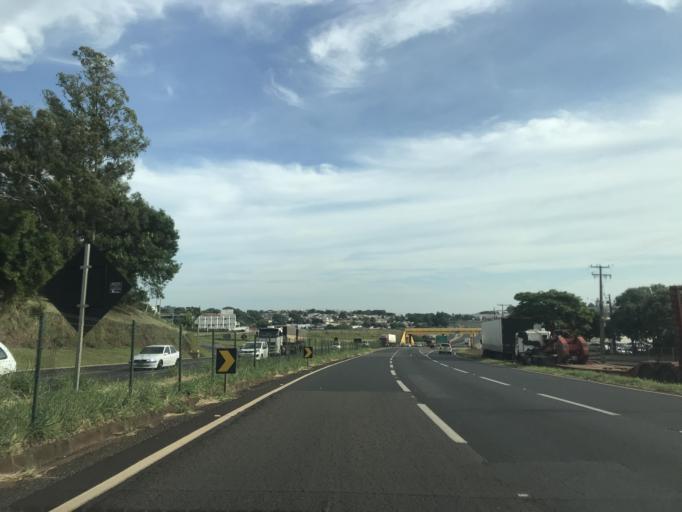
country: BR
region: Parana
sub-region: Mandaguacu
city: Mandaguacu
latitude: -23.3522
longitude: -52.0913
